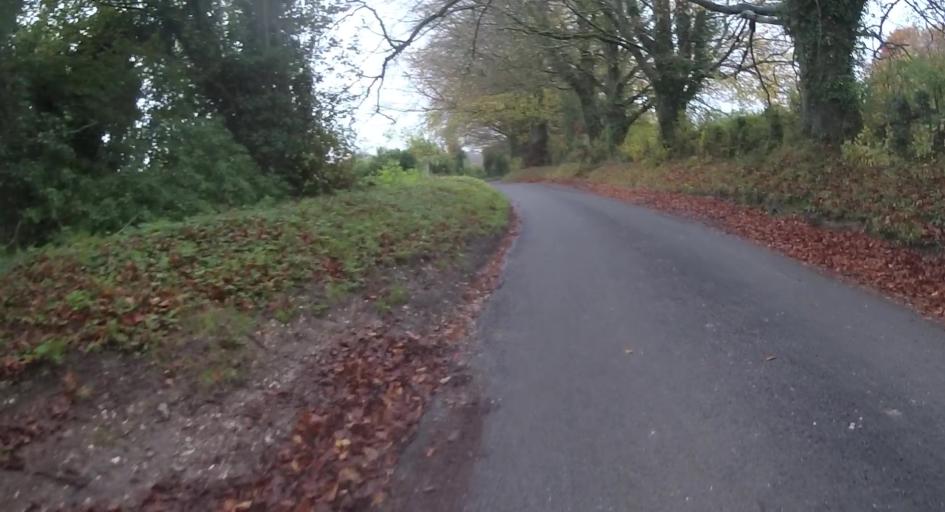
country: GB
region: England
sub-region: Hampshire
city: Four Marks
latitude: 51.1498
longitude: -1.1158
